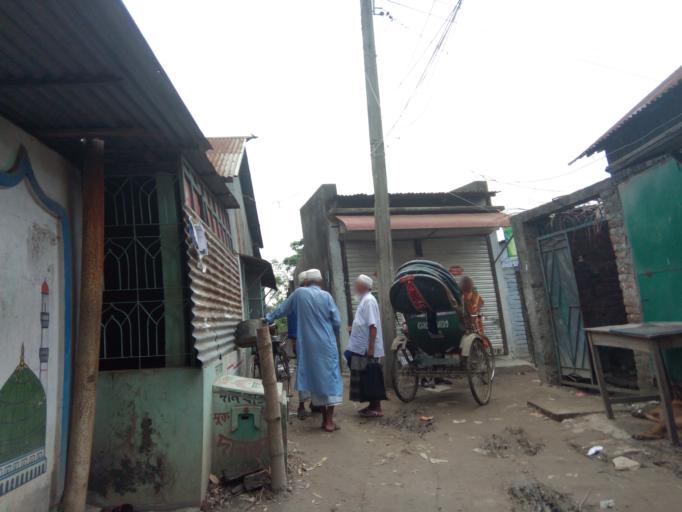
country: BD
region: Dhaka
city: Paltan
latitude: 23.7504
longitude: 90.4485
